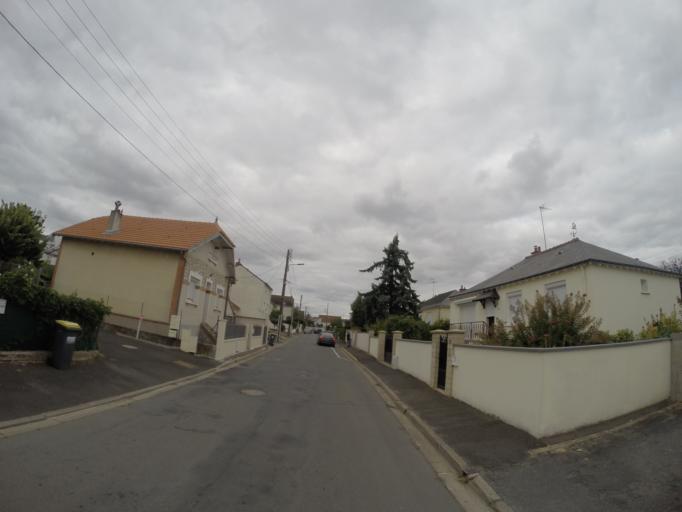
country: FR
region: Centre
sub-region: Departement d'Indre-et-Loire
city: Saint-Cyr-sur-Loire
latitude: 47.4159
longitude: 0.6917
